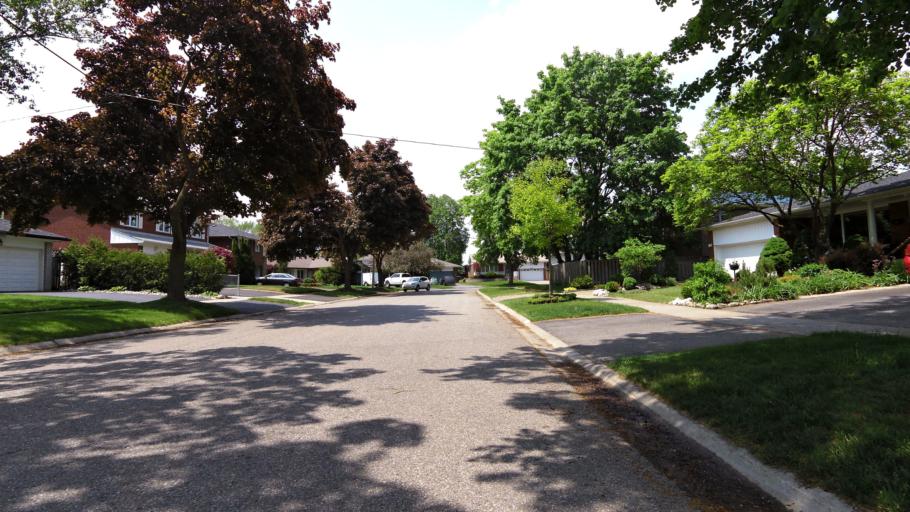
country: CA
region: Ontario
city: Etobicoke
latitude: 43.6056
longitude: -79.5666
